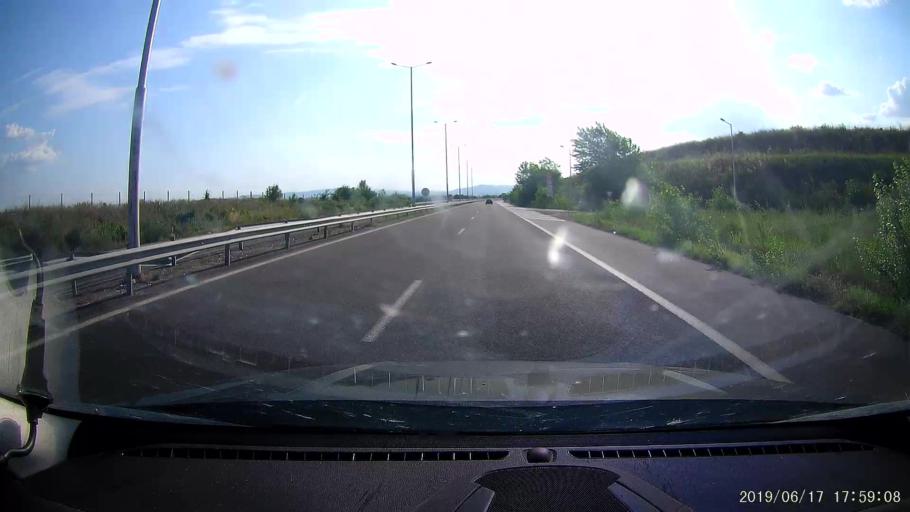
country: BG
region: Khaskovo
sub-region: Obshtina Svilengrad
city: Svilengrad
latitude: 41.7250
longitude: 26.3054
